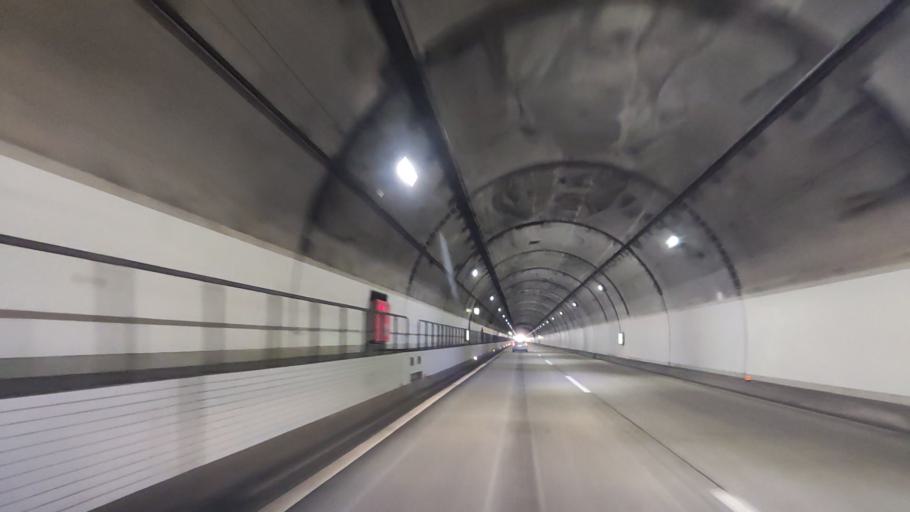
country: JP
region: Ehime
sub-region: Shikoku-chuo Shi
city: Matsuyama
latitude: 33.8239
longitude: 132.9709
